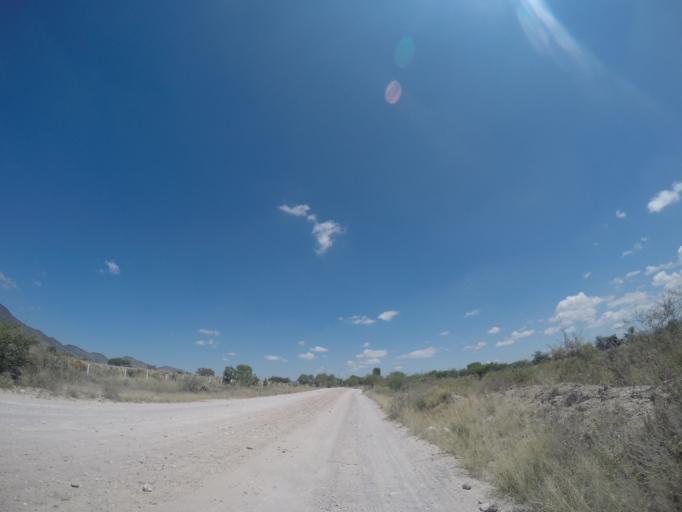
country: MX
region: San Luis Potosi
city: La Pila
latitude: 21.9945
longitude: -100.8988
